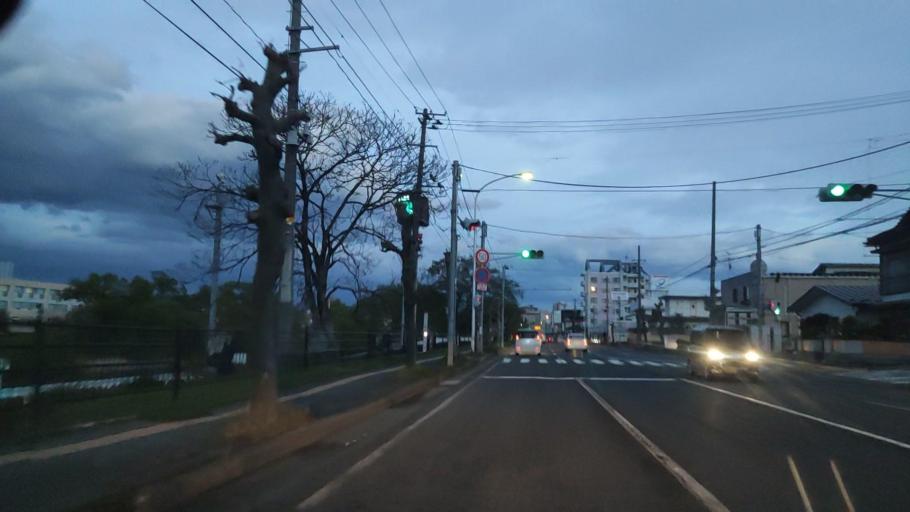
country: JP
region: Iwate
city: Morioka-shi
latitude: 39.7135
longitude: 141.1303
